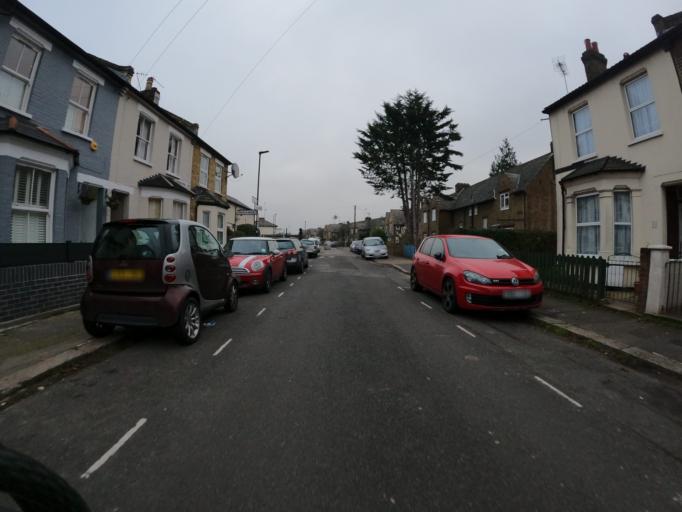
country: GB
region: England
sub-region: Greater London
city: Brentford
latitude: 51.4914
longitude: -0.3072
